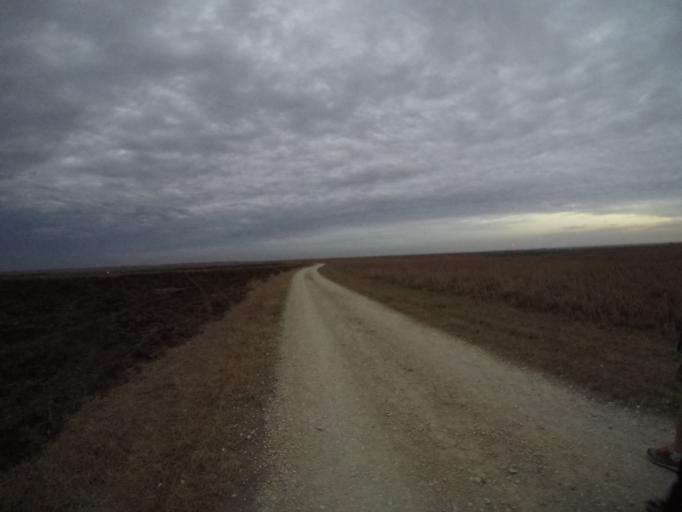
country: US
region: Kansas
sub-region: Chase County
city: Cottonwood Falls
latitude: 38.4368
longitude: -96.5755
